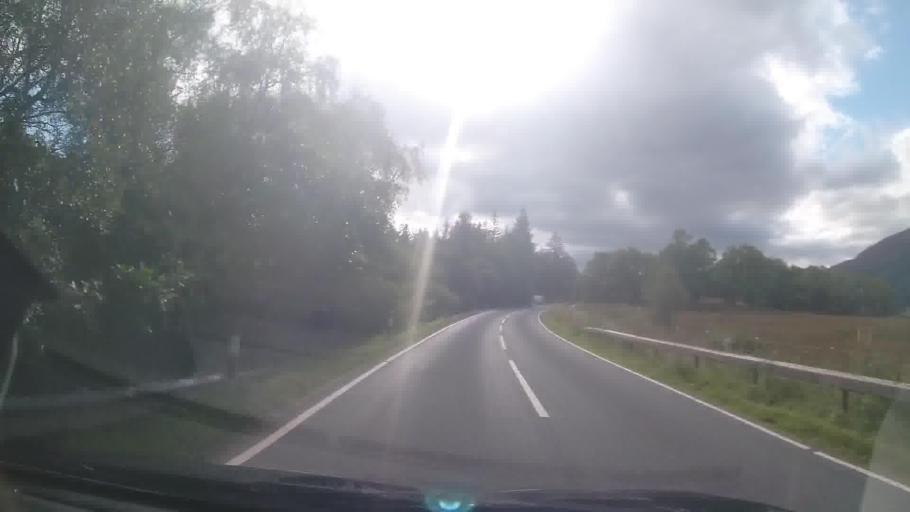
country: GB
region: Scotland
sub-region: Argyll and Bute
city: Garelochhead
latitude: 56.4042
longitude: -5.0132
